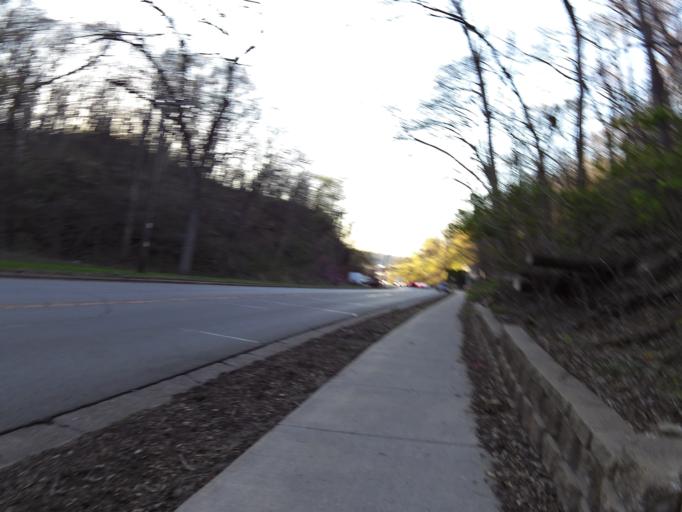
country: US
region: Wisconsin
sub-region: Saint Croix County
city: Hudson
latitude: 44.9689
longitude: -92.7530
